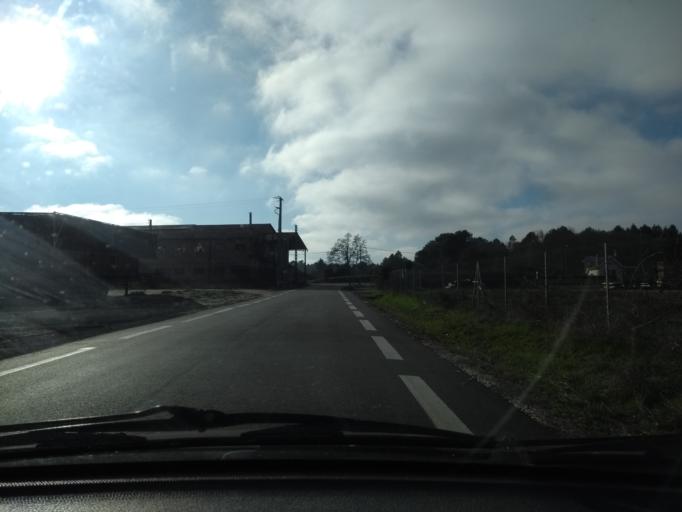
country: FR
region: Aquitaine
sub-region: Departement de la Gironde
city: Salles
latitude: 44.5575
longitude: -0.8712
